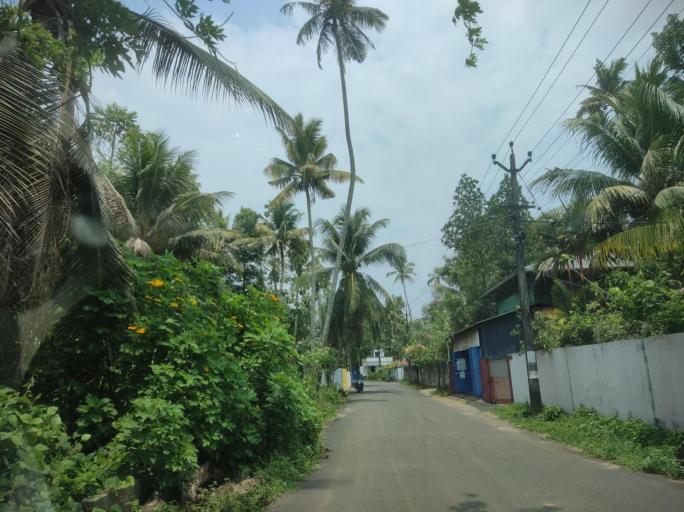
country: IN
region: Kerala
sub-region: Alappuzha
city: Vayalar
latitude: 9.7324
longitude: 76.3280
